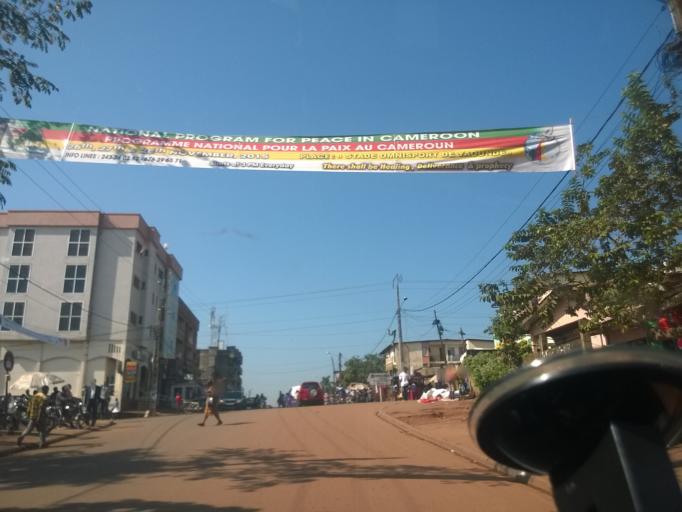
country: CM
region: Centre
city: Yaounde
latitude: 3.8411
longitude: 11.4887
